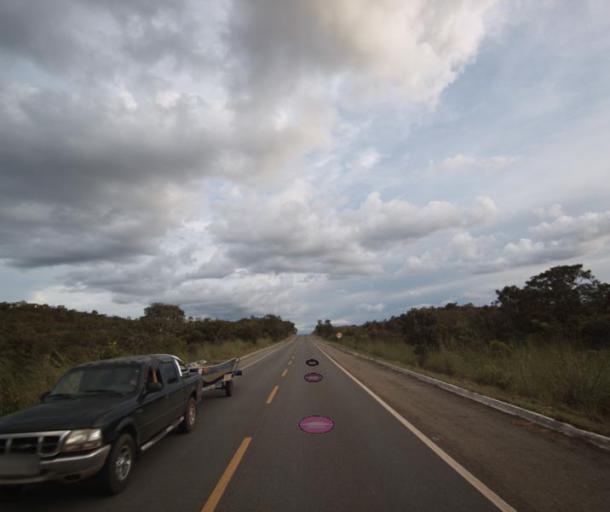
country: BR
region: Goias
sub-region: Barro Alto
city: Barro Alto
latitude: -14.9016
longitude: -48.6437
